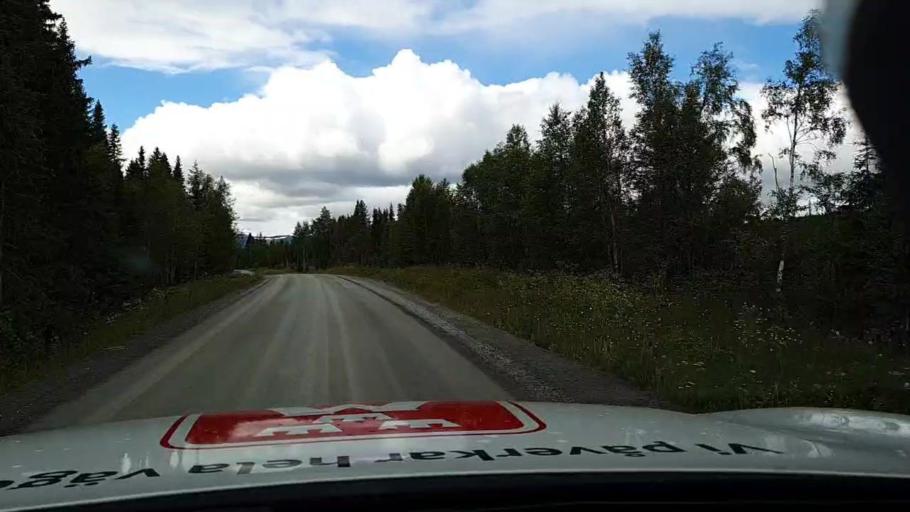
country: SE
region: Jaemtland
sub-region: Krokoms Kommun
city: Valla
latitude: 63.6904
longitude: 13.6718
